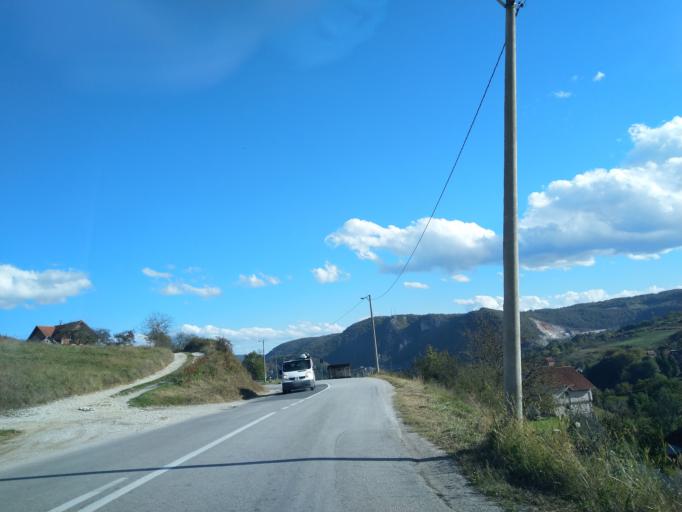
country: RS
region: Central Serbia
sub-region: Zlatiborski Okrug
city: Uzice
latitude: 43.8659
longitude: 19.8069
